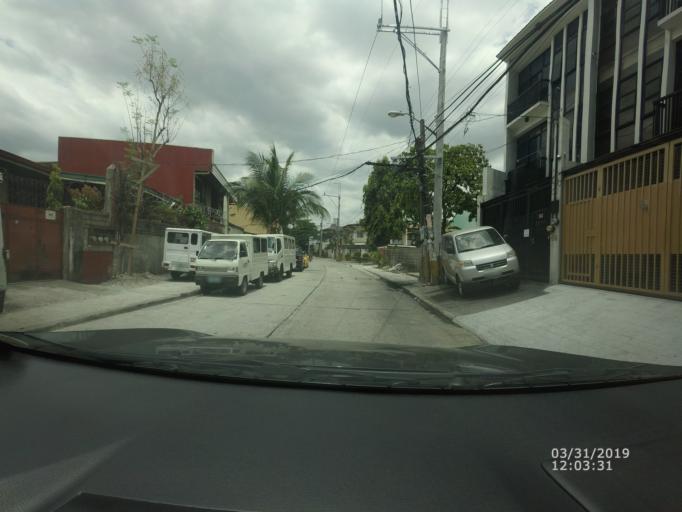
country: PH
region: Metro Manila
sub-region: Mandaluyong
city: Mandaluyong City
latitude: 14.5768
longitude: 121.0367
